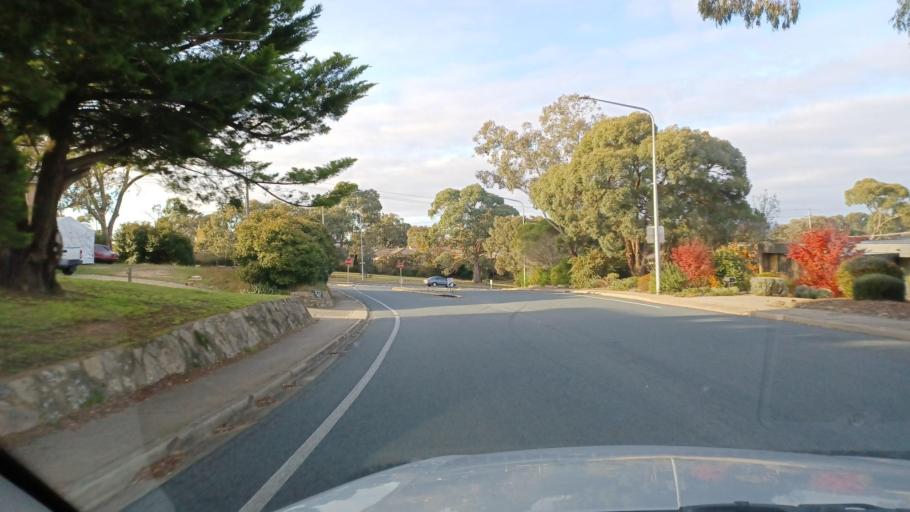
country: AU
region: Australian Capital Territory
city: Belconnen
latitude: -35.2033
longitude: 149.0502
